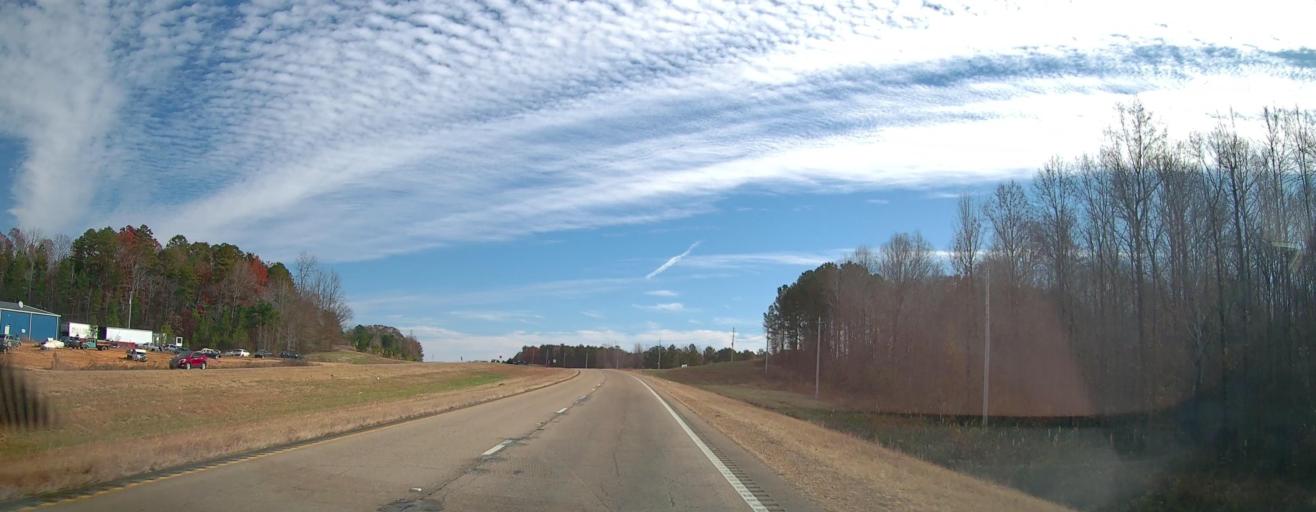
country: US
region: Mississippi
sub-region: Alcorn County
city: Corinth
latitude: 34.9324
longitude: -88.7194
